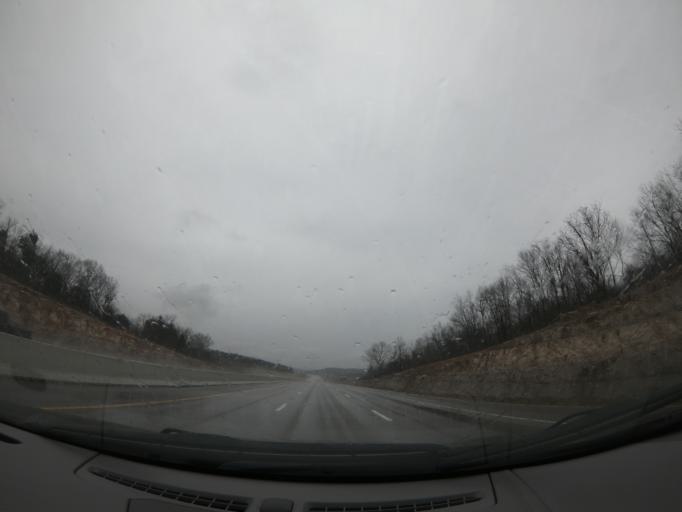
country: US
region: Kentucky
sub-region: Hart County
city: Horse Cave
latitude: 37.2276
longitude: -85.9317
